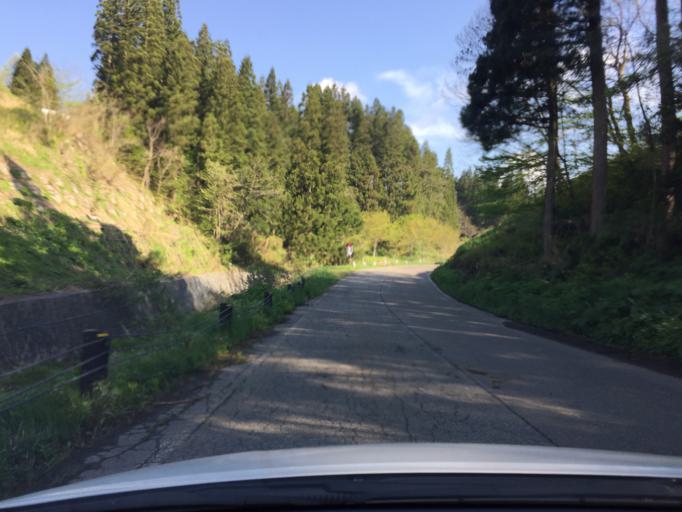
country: JP
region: Fukushima
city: Kitakata
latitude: 37.6886
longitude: 139.7169
